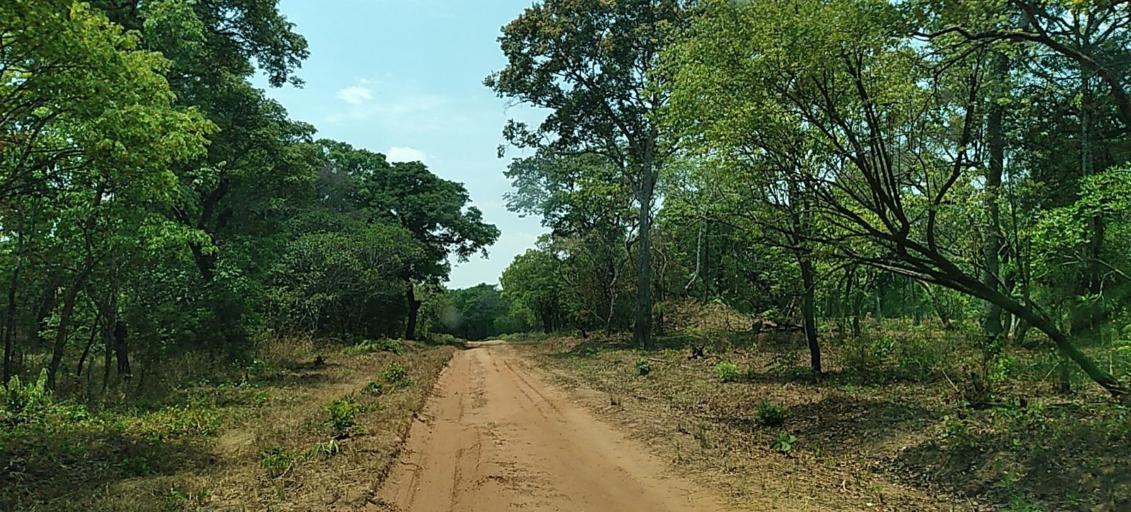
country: CD
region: Katanga
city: Kolwezi
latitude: -11.3510
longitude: 25.2133
